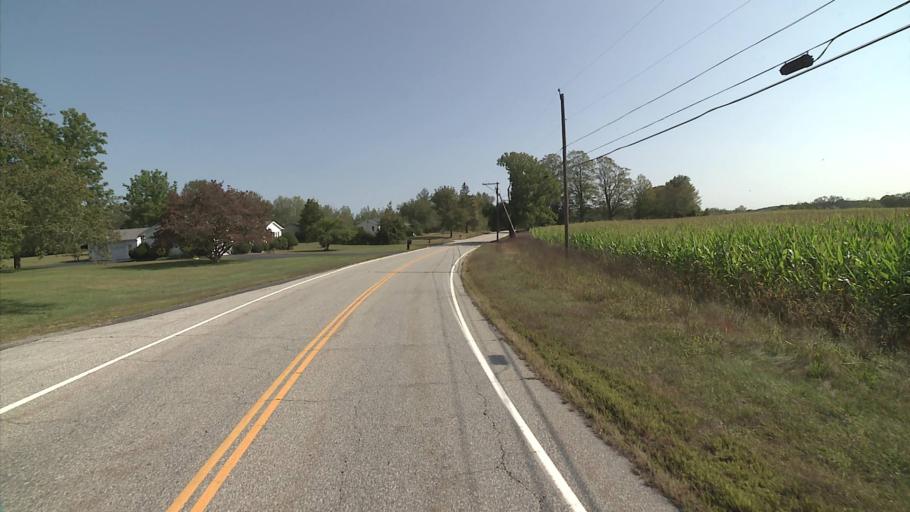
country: US
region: Connecticut
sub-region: Windham County
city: Plainfield Village
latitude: 41.6763
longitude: -71.9724
